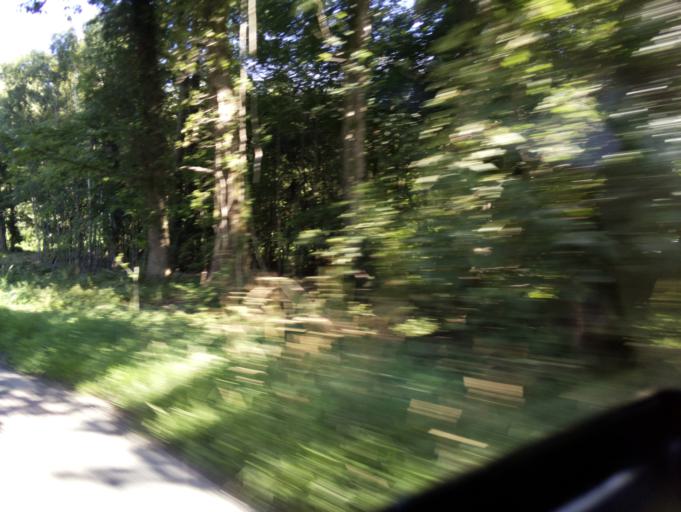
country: GB
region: England
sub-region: Gloucestershire
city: Coleford
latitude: 51.8010
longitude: -2.6333
